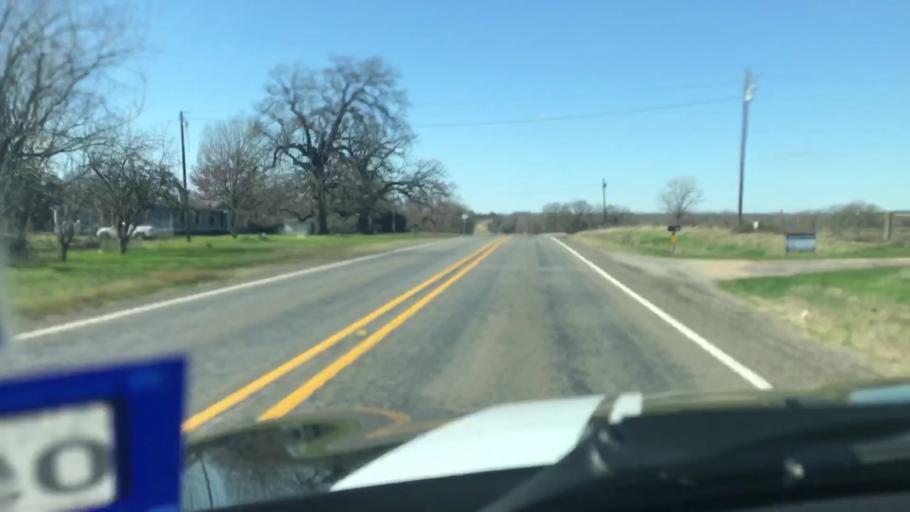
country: US
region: Texas
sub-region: Robertson County
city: Calvert
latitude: 30.8848
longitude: -96.7554
